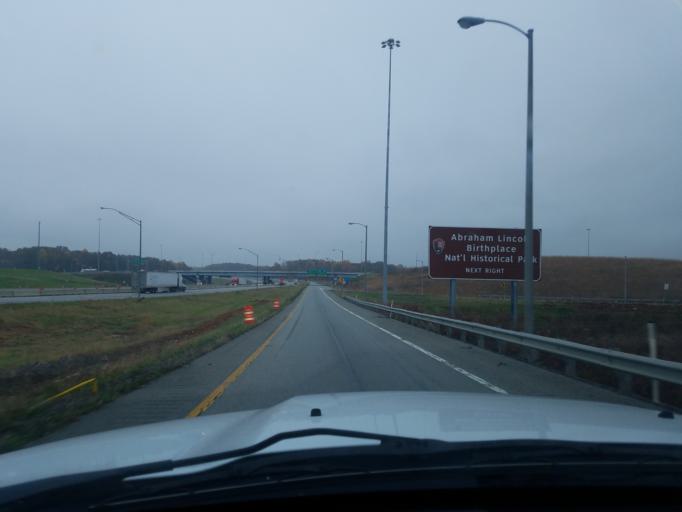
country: US
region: Kentucky
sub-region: Hardin County
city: Elizabethtown
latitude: 37.6766
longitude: -85.8489
